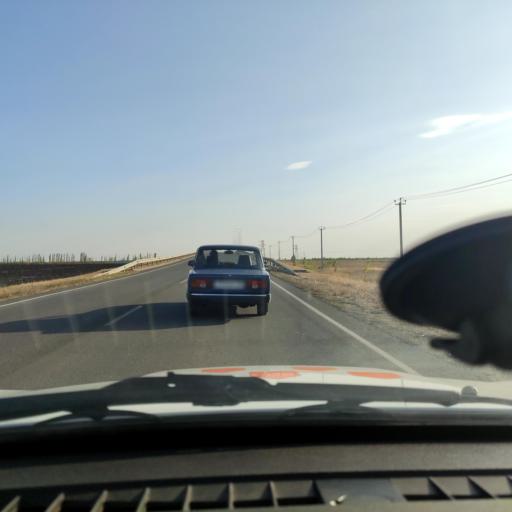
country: RU
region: Voronezj
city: Novaya Usman'
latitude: 51.5952
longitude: 39.3737
